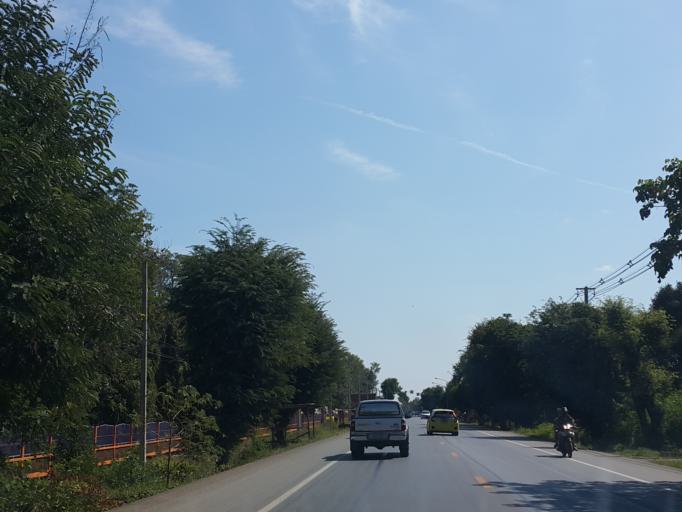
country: TH
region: Sukhothai
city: Sawankhalok
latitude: 17.2617
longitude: 99.8461
